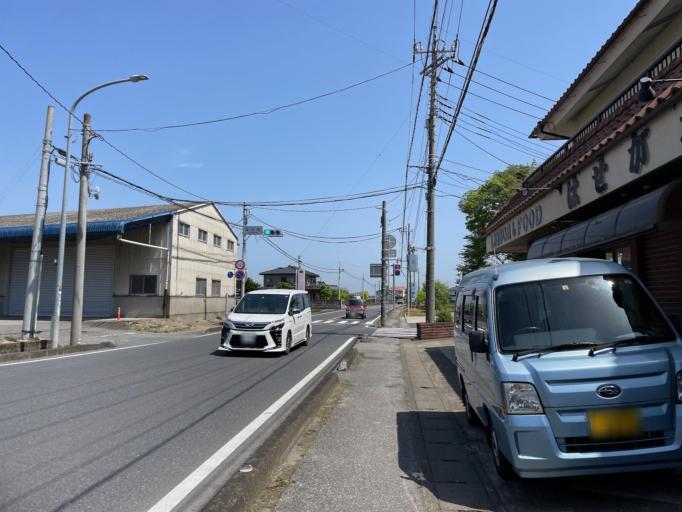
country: JP
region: Tochigi
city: Ashikaga
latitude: 36.3047
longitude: 139.4797
